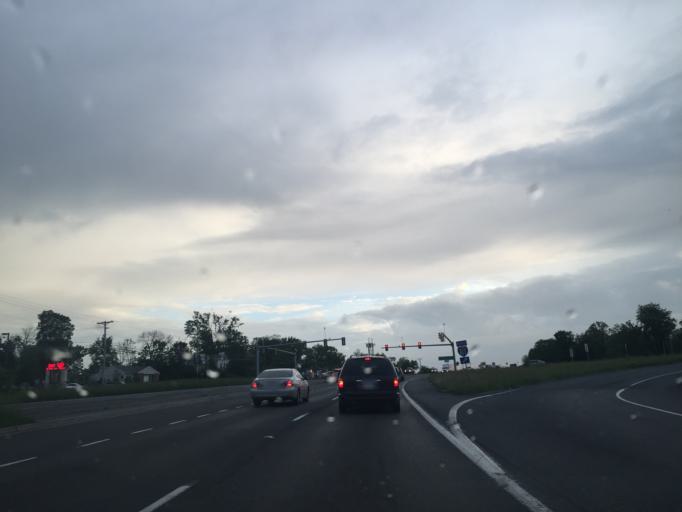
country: US
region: Virginia
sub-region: City of Winchester
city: Winchester
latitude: 39.1850
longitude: -78.1331
